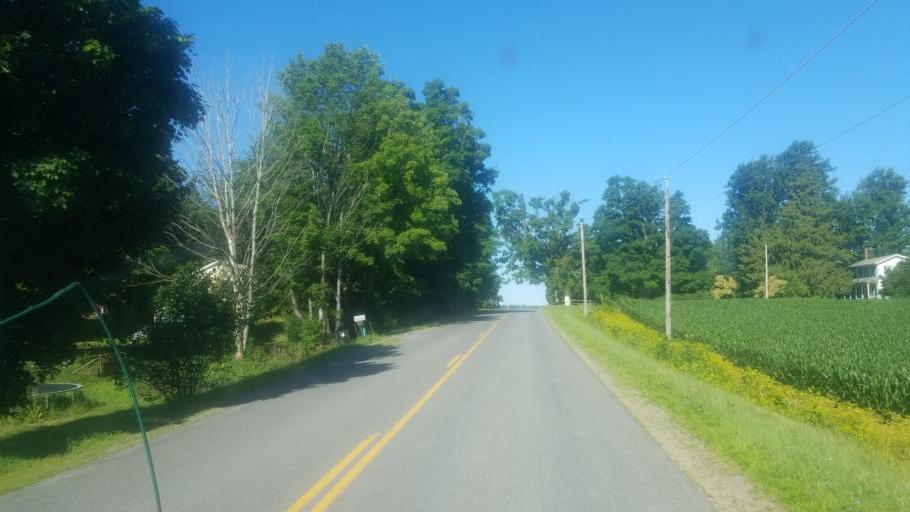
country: US
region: New York
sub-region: Ontario County
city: Clifton Springs
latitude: 42.8386
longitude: -77.1327
